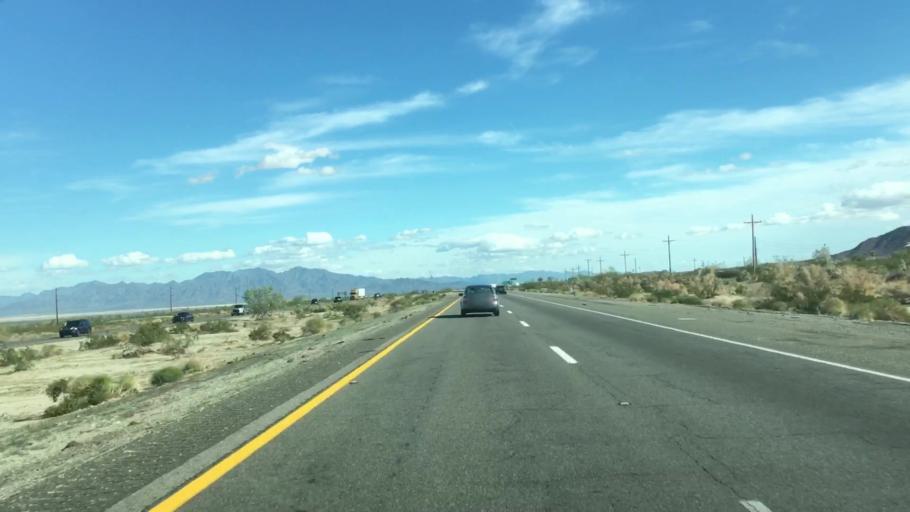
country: US
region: California
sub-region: Imperial County
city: Niland
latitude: 33.7105
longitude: -115.3854
